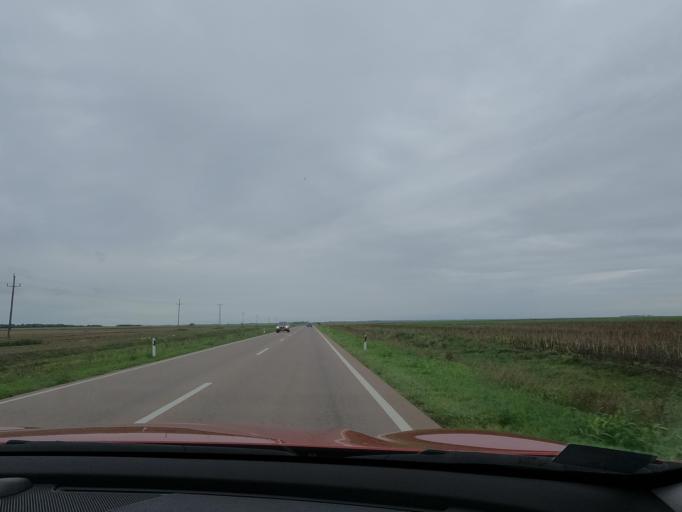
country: RS
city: Banatska Topola
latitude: 45.7323
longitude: 20.4198
